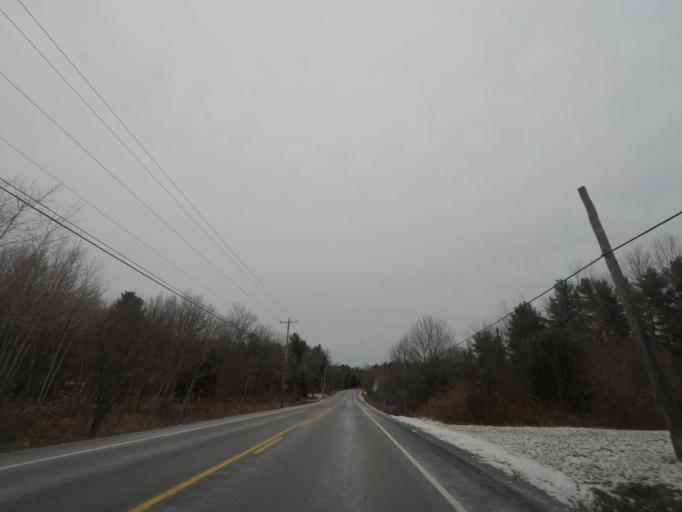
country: US
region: New York
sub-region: Rensselaer County
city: Hoosick Falls
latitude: 42.7699
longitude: -73.4249
